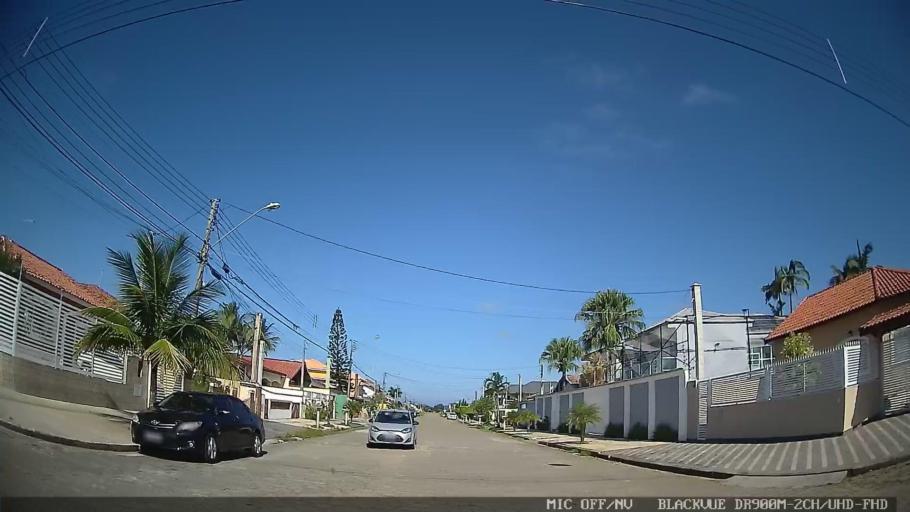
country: BR
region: Sao Paulo
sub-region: Peruibe
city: Peruibe
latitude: -24.2871
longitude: -46.9634
